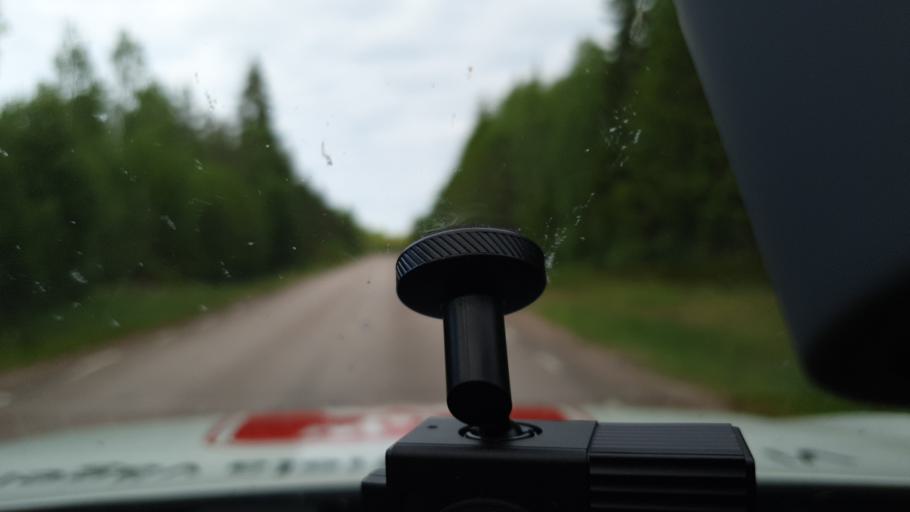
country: SE
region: Vaermland
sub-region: Torsby Kommun
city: Torsby
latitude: 60.1095
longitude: 12.9119
